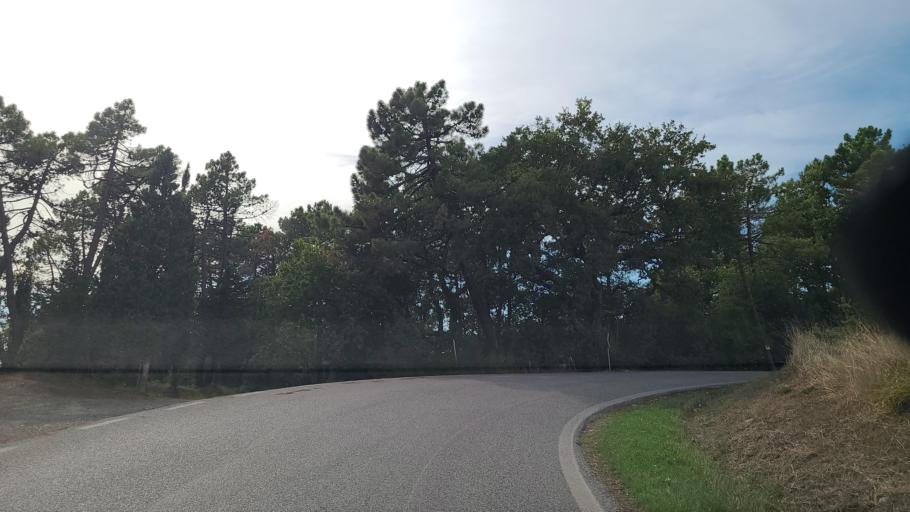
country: IT
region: Tuscany
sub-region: Provincia di Siena
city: San Gimignano
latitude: 43.4281
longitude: 10.9707
